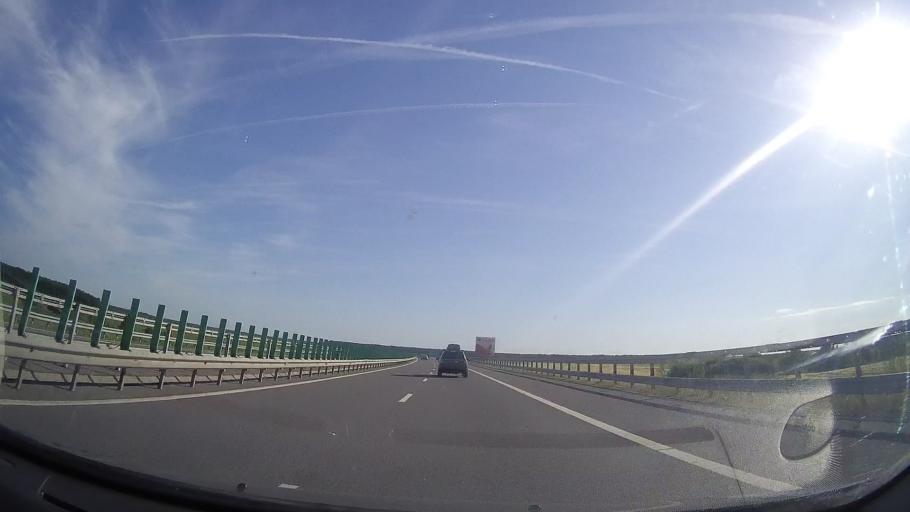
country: RO
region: Ilfov
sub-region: Comuna Gruiu
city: Gruiu
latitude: 44.7058
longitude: 26.2281
